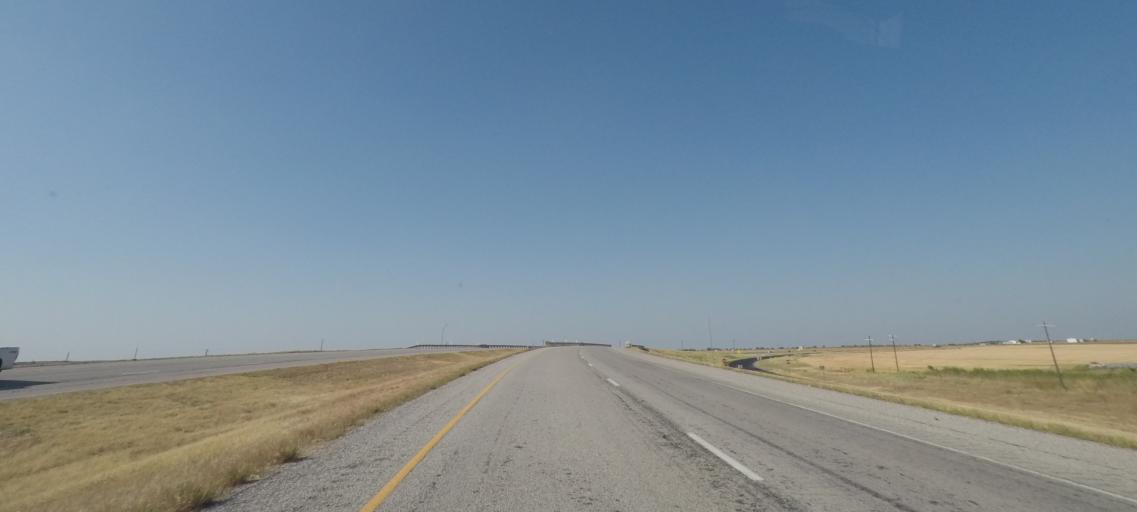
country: US
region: Texas
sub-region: Baylor County
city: Seymour
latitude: 33.6136
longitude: -99.2431
